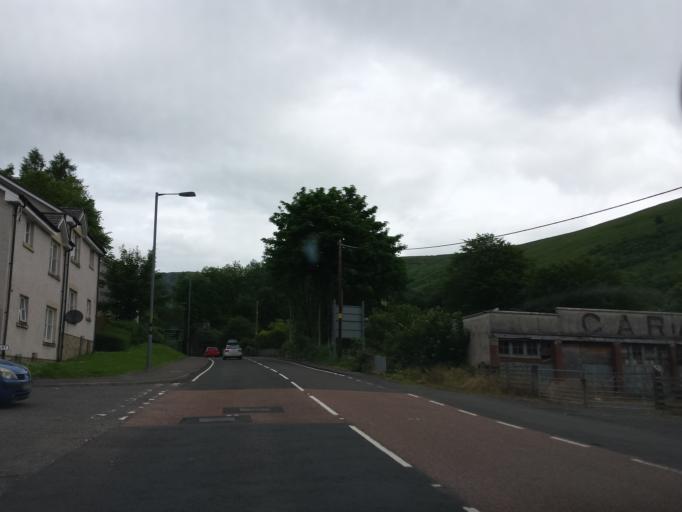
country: GB
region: Scotland
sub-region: Stirling
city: Callander
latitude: 56.3860
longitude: -4.2877
